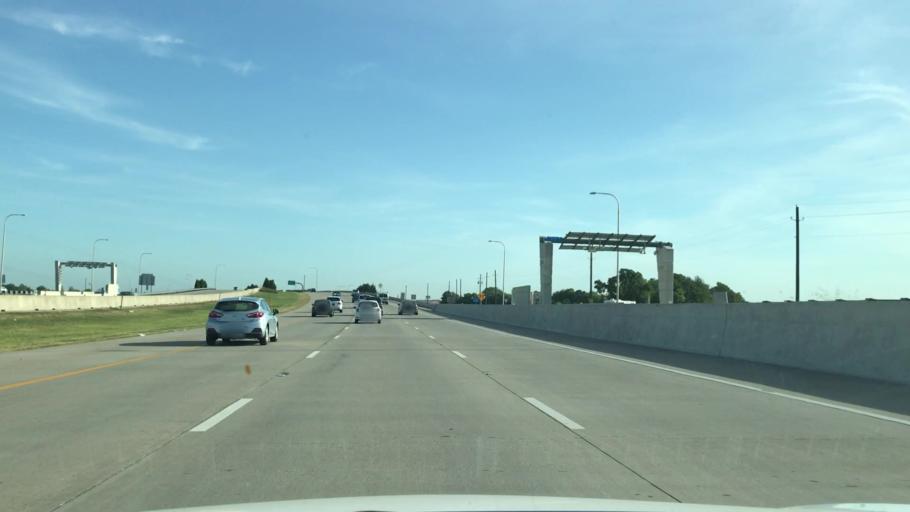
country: US
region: Texas
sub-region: Dallas County
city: Rowlett
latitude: 32.9278
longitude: -96.5523
